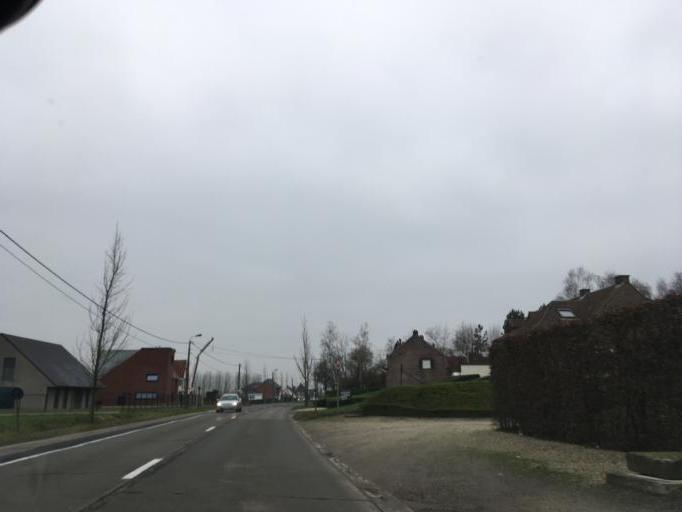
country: BE
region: Flanders
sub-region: Provincie West-Vlaanderen
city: Anzegem
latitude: 50.8573
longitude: 3.4536
